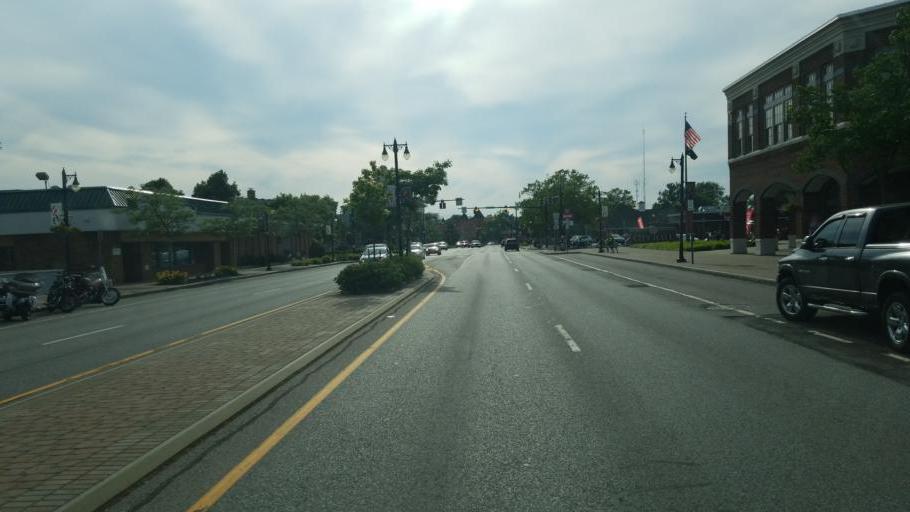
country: US
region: New York
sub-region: Genesee County
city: Batavia
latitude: 42.9977
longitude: -78.1842
